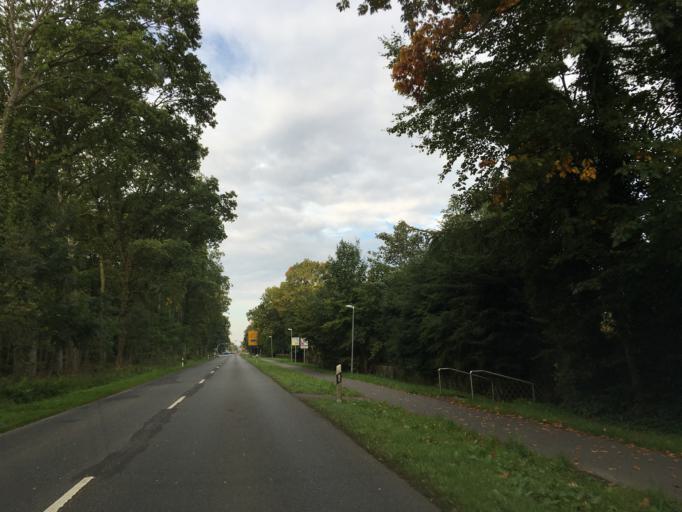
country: DE
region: Lower Saxony
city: Adendorf
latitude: 53.2607
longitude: 10.4496
